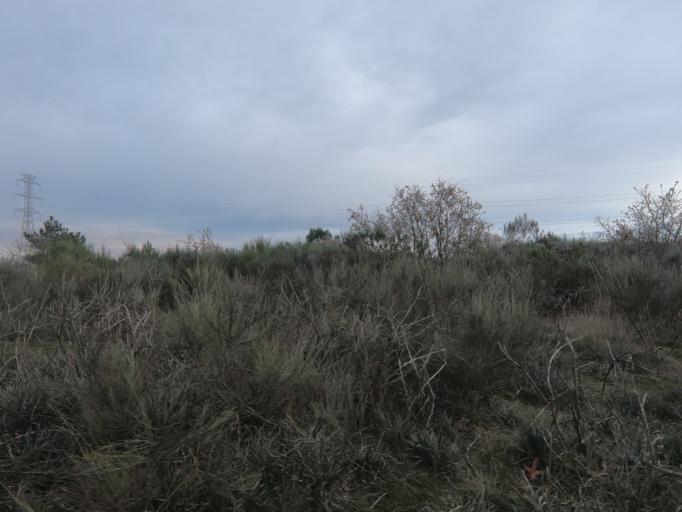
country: PT
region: Vila Real
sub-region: Sabrosa
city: Sabrosa
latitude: 41.3184
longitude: -7.6302
